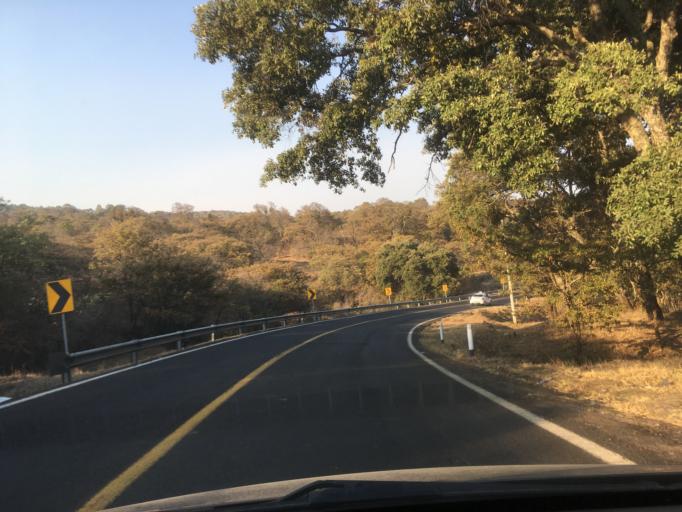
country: MX
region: Michoacan
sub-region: Morelia
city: Iratzio
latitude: 19.6303
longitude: -101.4430
